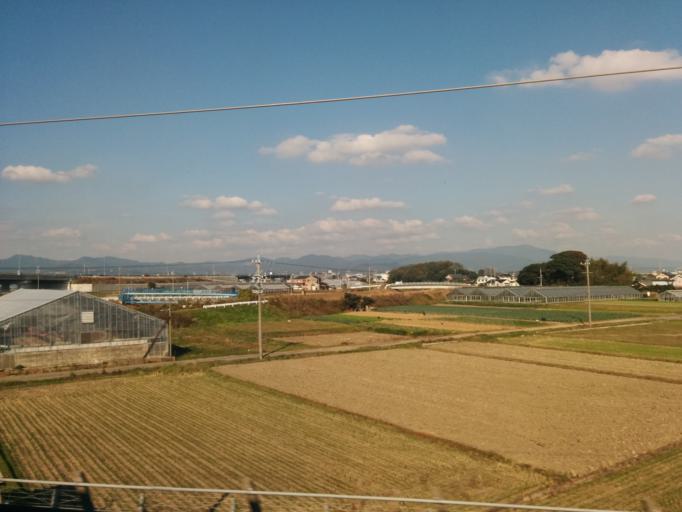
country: JP
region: Aichi
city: Kozakai-cho
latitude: 34.7958
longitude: 137.3346
